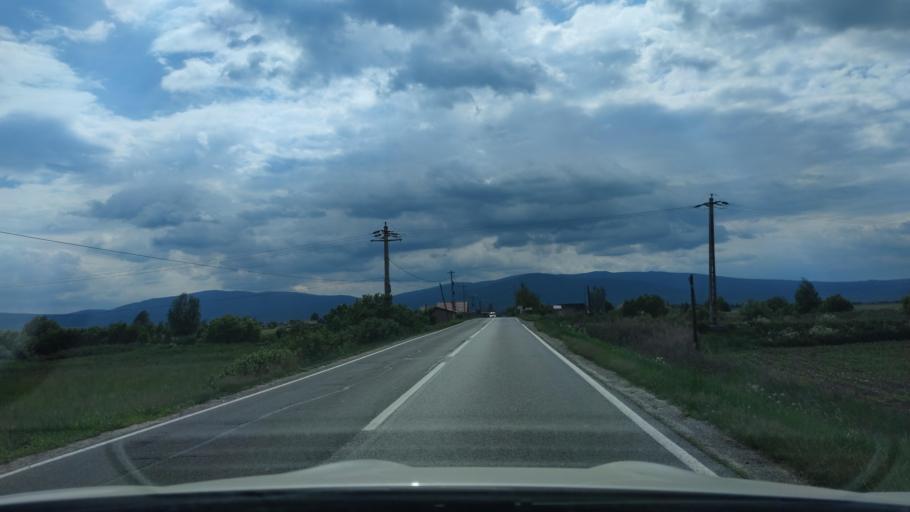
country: RO
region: Harghita
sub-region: Comuna Joseni
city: Joseni
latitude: 46.6974
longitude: 25.4776
